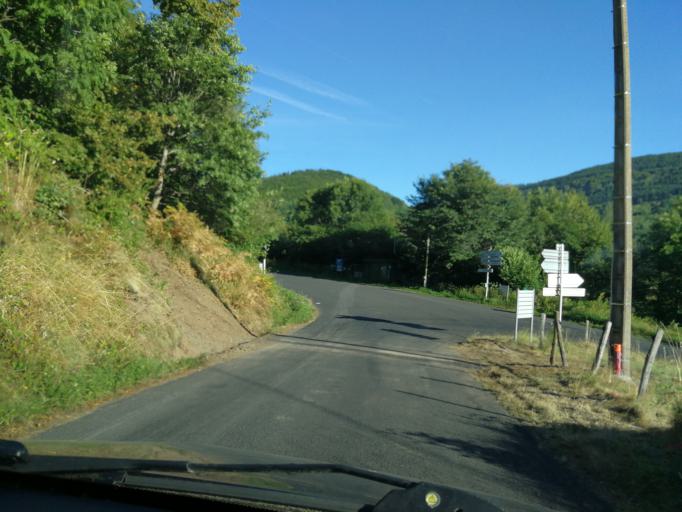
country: FR
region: Auvergne
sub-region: Departement du Cantal
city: Vic-sur-Cere
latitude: 45.0905
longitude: 2.5631
